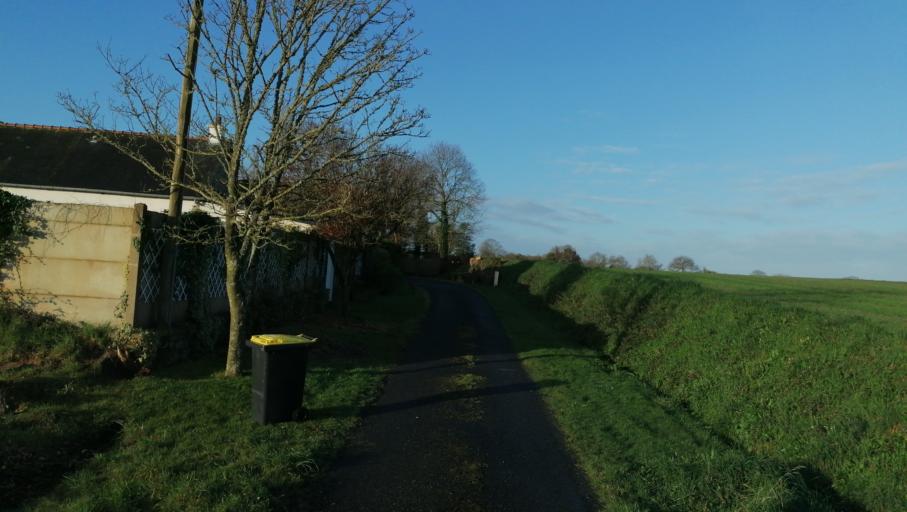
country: FR
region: Brittany
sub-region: Departement des Cotes-d'Armor
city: Plouha
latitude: 48.6644
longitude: -2.9155
